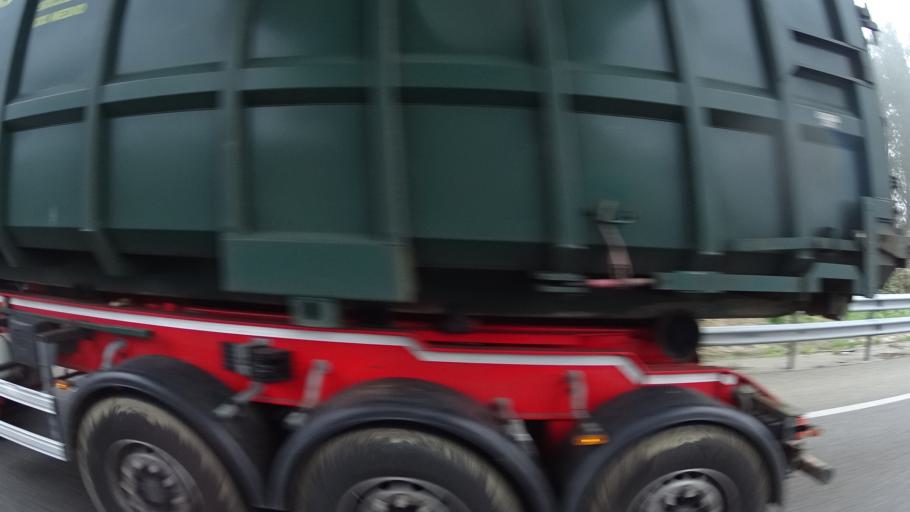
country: ES
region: Galicia
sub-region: Provincia de Lugo
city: Guitiriz
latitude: 43.1897
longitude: -7.8626
